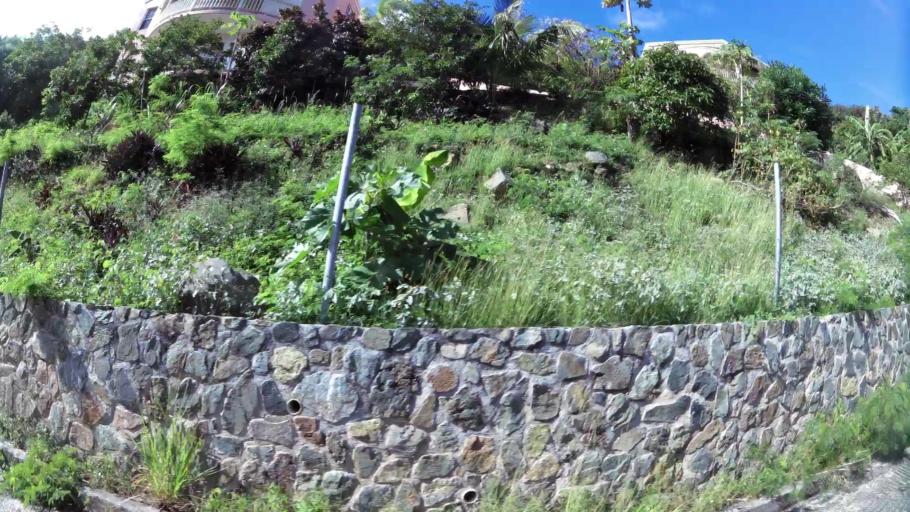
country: VG
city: Tortola
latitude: 18.4344
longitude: -64.5778
